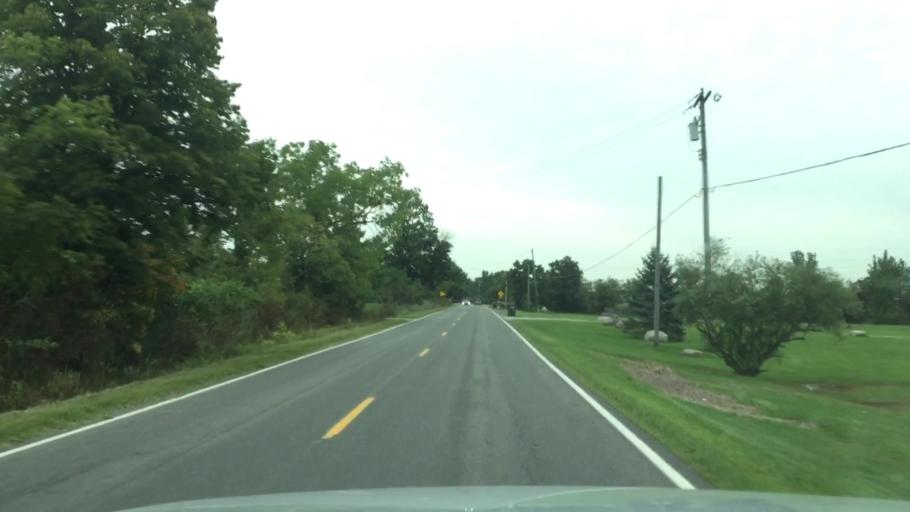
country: US
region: Michigan
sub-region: Washtenaw County
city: Milan
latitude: 42.1398
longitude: -83.6664
